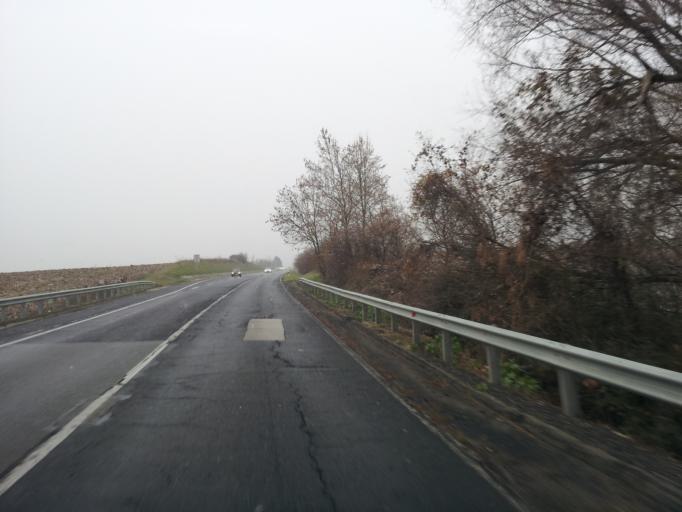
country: HU
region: Veszprem
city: Herend
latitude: 47.1436
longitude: 17.6829
